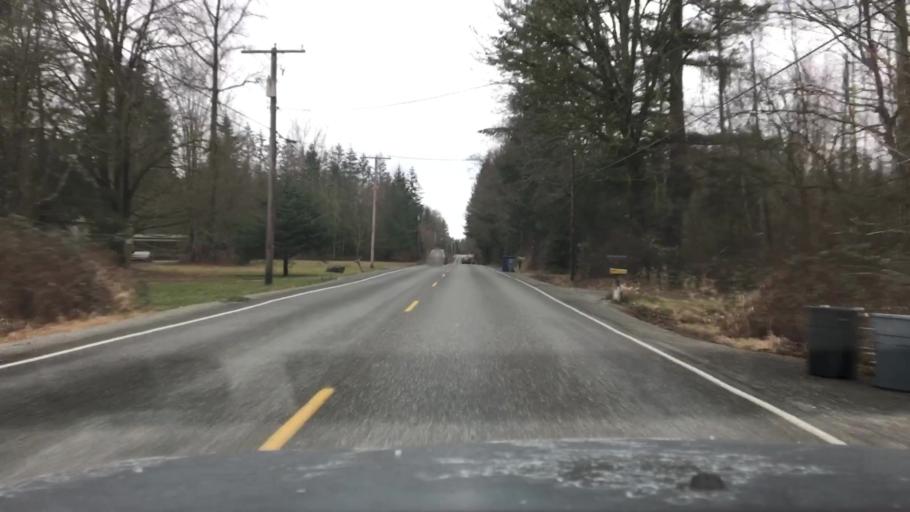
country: US
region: Washington
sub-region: Whatcom County
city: Sudden Valley
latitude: 48.6283
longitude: -122.3195
